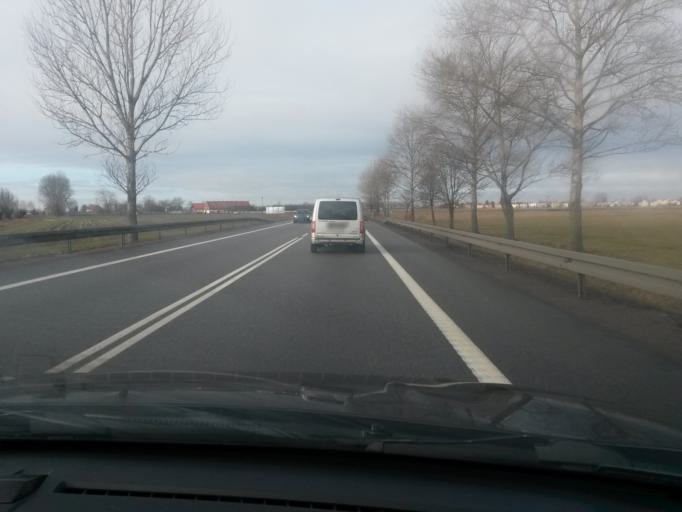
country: PL
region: Pomeranian Voivodeship
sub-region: Powiat nowodworski
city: Nowy Dwor Gdanski
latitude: 54.1965
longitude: 19.1307
